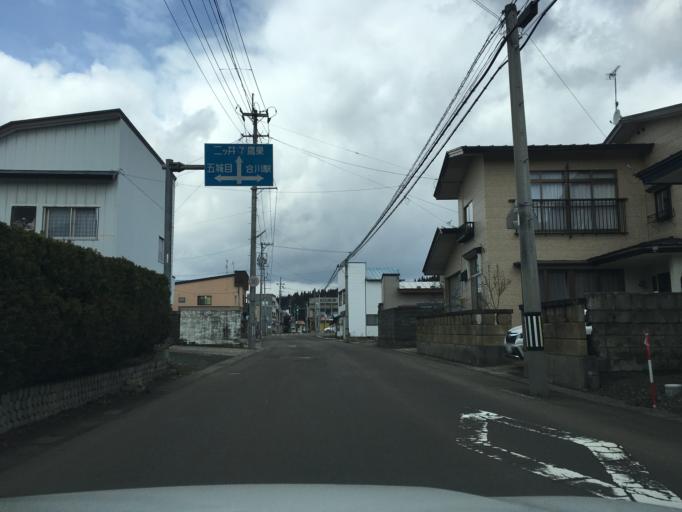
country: JP
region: Akita
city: Takanosu
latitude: 40.1601
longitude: 140.3311
